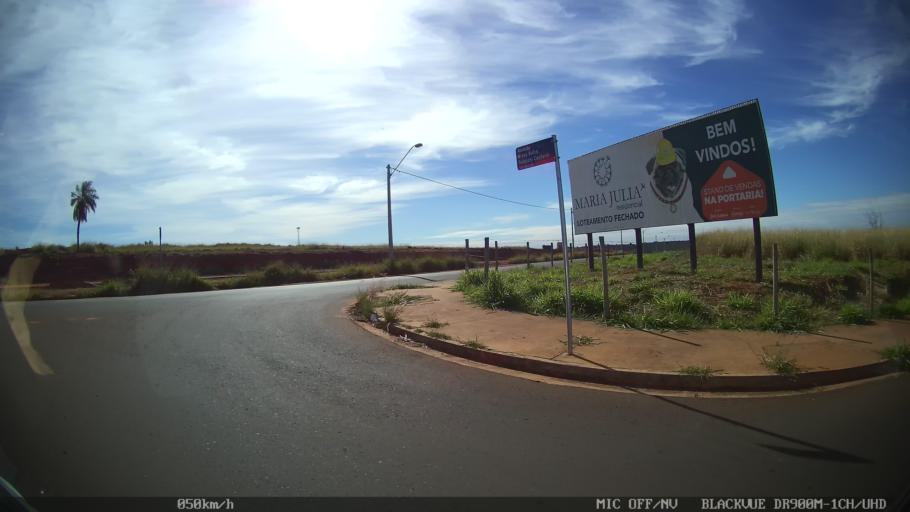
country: BR
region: Sao Paulo
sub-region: Sao Jose Do Rio Preto
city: Sao Jose do Rio Preto
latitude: -20.8052
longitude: -49.3261
